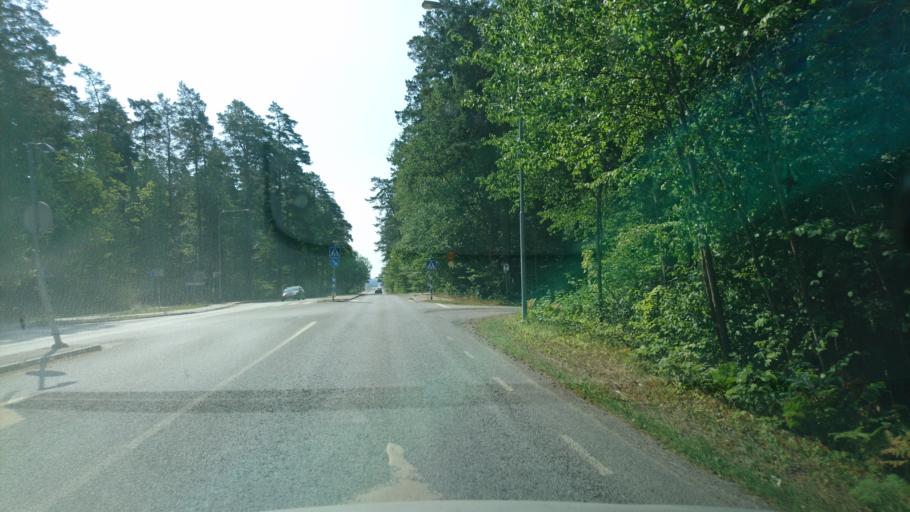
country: SE
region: Uppsala
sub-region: Uppsala Kommun
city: Uppsala
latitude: 59.8283
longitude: 17.6441
